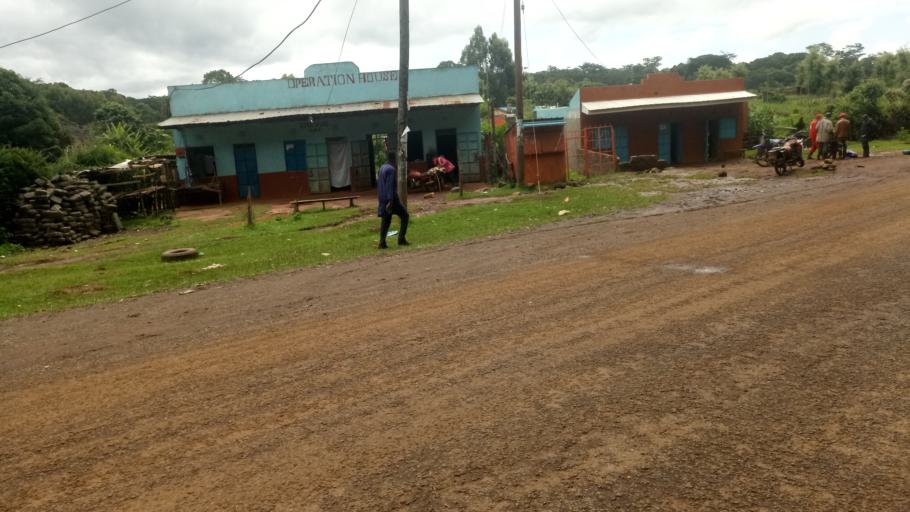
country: KE
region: Kirinyaga
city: Keruguya
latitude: -0.3915
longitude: 37.1620
